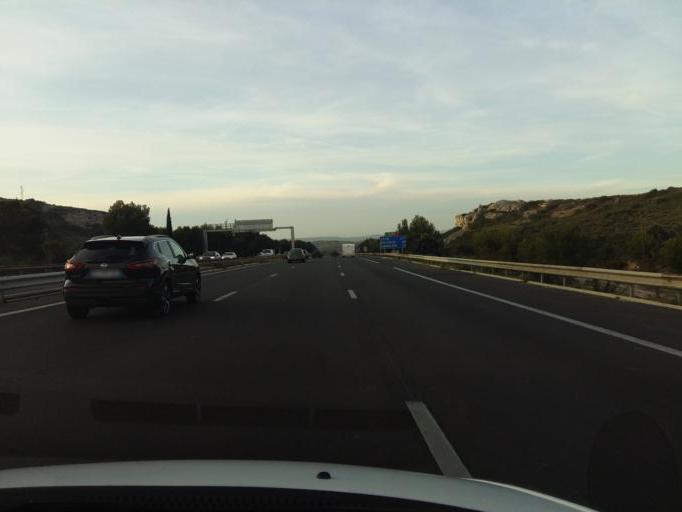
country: FR
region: Provence-Alpes-Cote d'Azur
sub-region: Departement des Bouches-du-Rhone
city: La Fare-les-Oliviers
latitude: 43.5735
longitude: 5.2137
